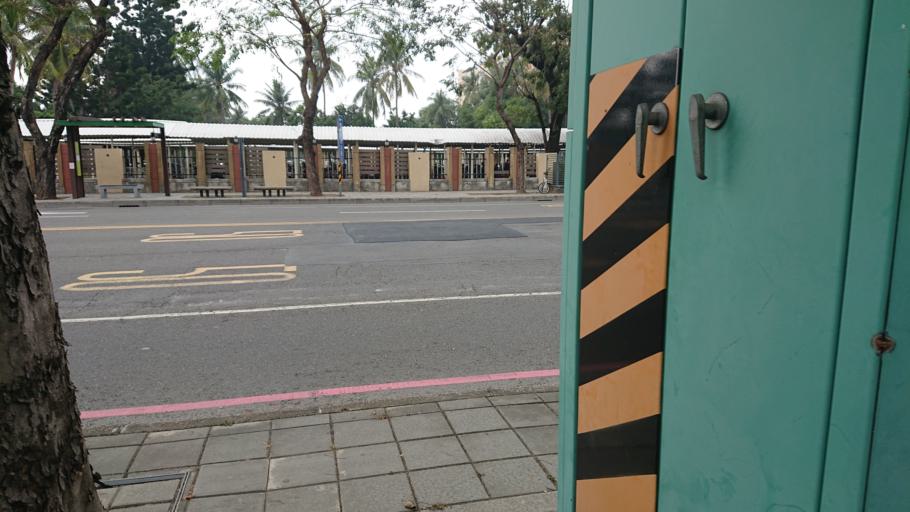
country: TW
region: Kaohsiung
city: Kaohsiung
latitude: 22.7011
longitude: 120.2926
